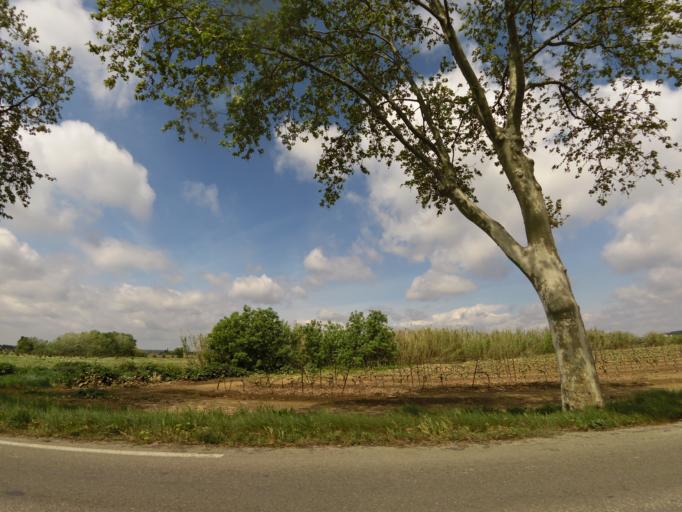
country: FR
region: Languedoc-Roussillon
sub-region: Departement du Gard
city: Mus
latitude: 43.7108
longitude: 4.1967
